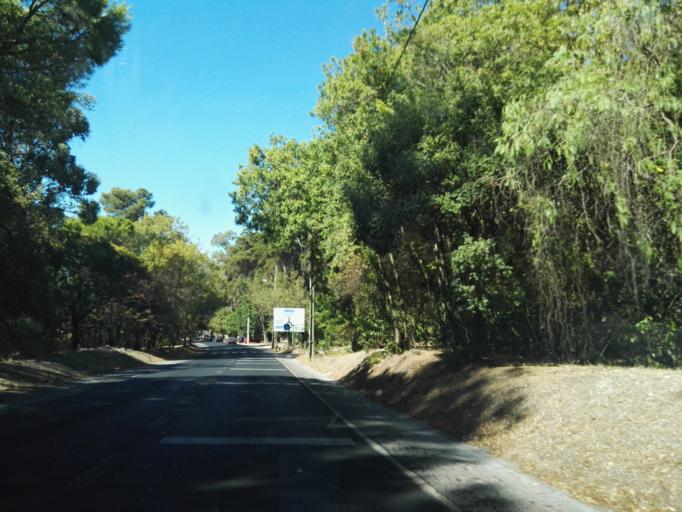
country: PT
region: Lisbon
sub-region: Odivelas
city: Pontinha
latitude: 38.7351
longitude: -9.1997
